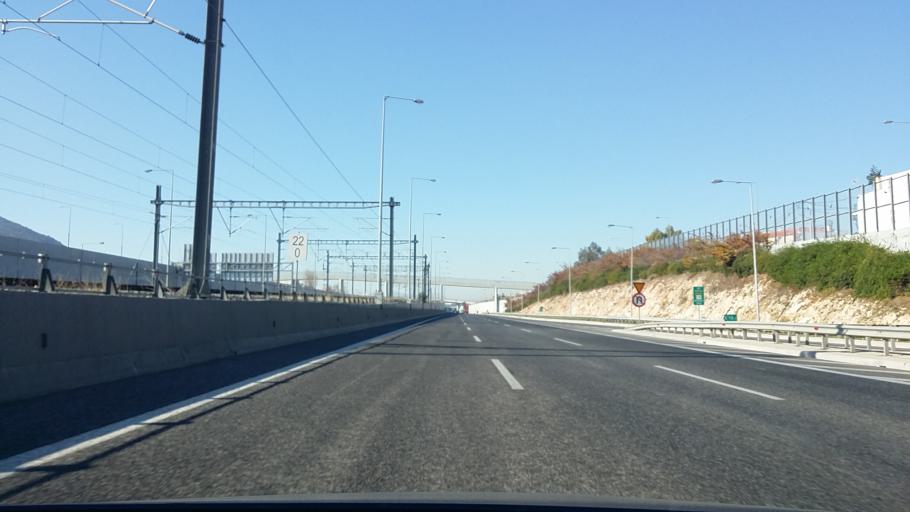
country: GR
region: Attica
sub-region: Nomarchia Dytikis Attikis
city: Zefyri
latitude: 38.0714
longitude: 23.7069
